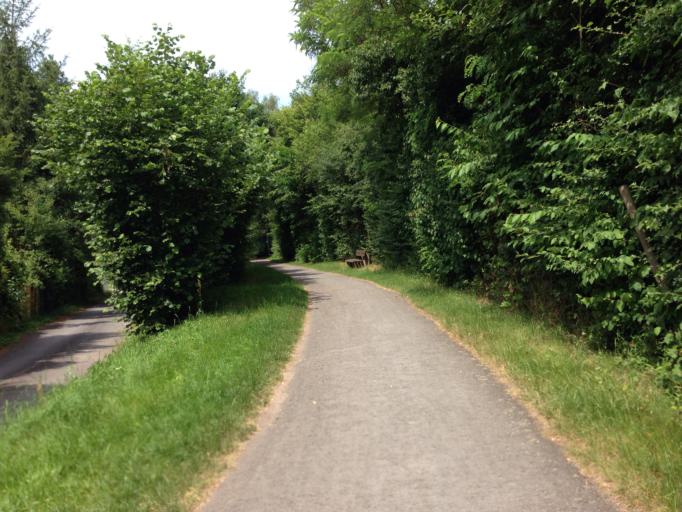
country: DE
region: Bavaria
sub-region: Regierungsbezirk Unterfranken
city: Kahl am Main
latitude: 50.0662
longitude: 8.9925
